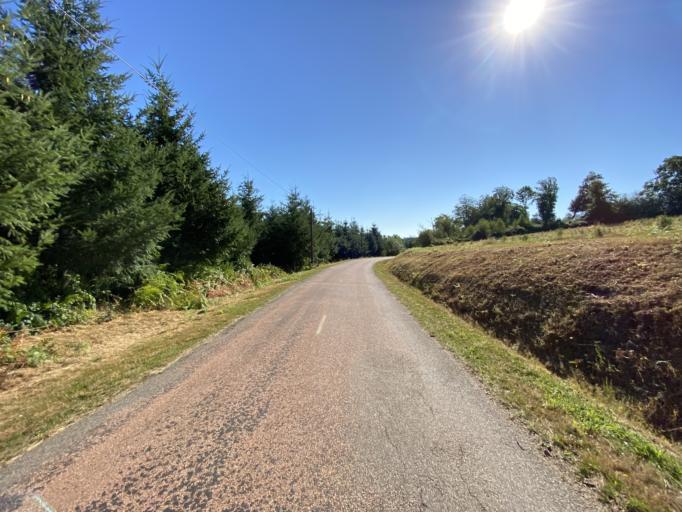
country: FR
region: Bourgogne
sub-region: Departement de la Cote-d'Or
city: Saulieu
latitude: 47.2725
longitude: 4.1670
